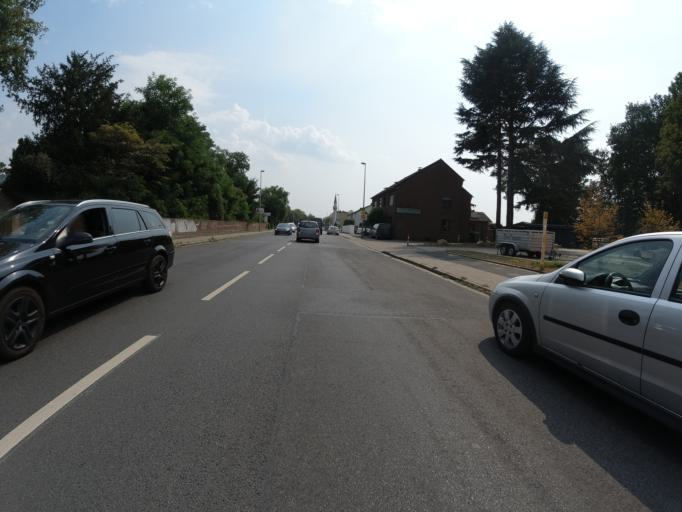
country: DE
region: North Rhine-Westphalia
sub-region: Regierungsbezirk Dusseldorf
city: Moers
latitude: 51.4589
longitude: 6.6536
